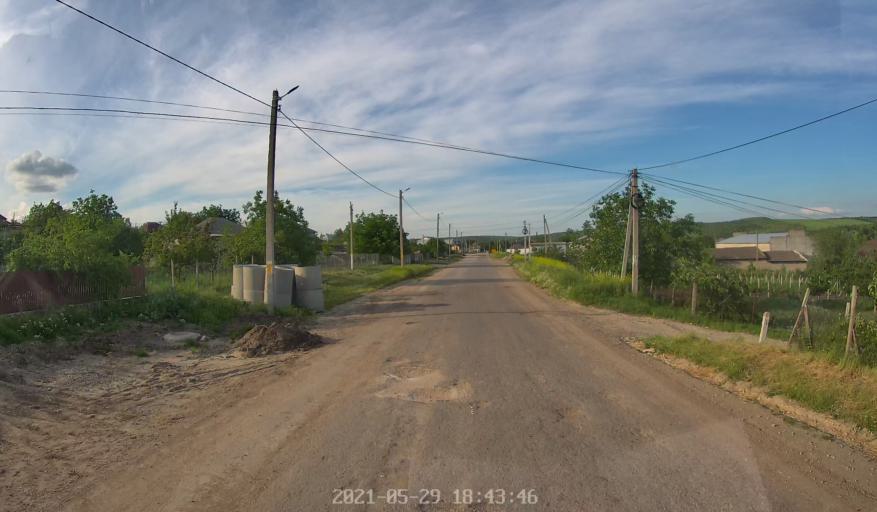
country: MD
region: Chisinau
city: Singera
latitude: 46.8204
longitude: 28.9660
